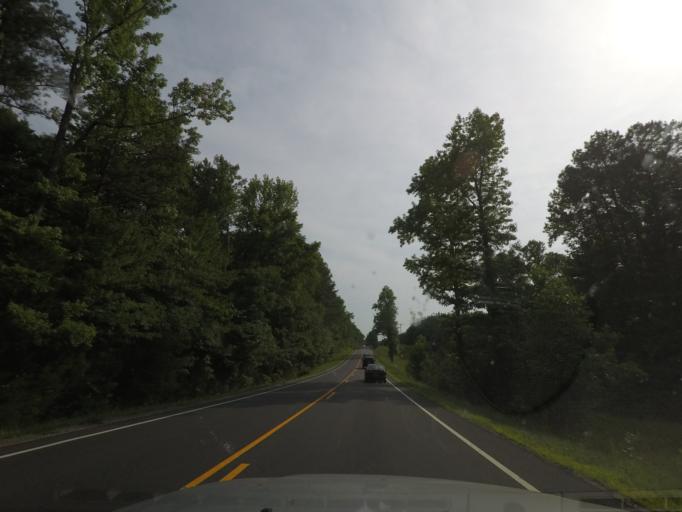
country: US
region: Virginia
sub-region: Prince Edward County
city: Hampden Sydney
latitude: 37.1173
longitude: -78.4599
